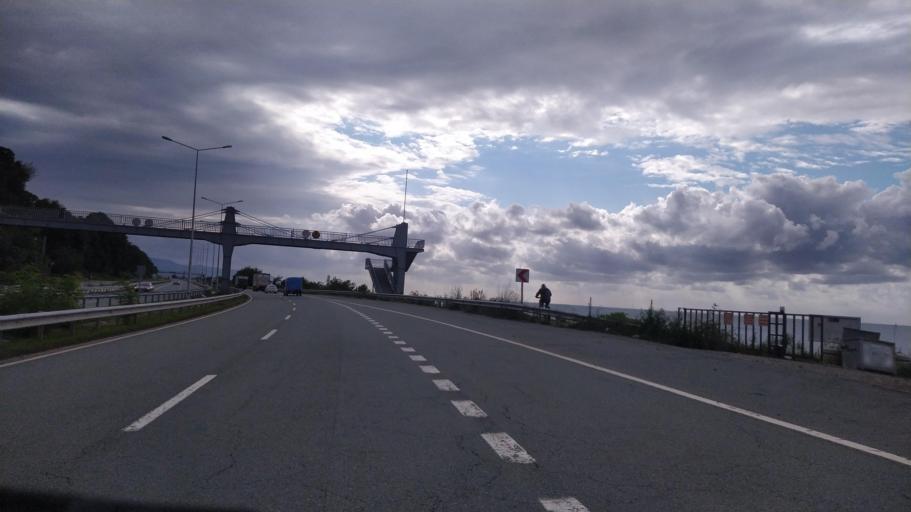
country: TR
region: Rize
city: Ardesen
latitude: 41.2102
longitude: 41.0370
